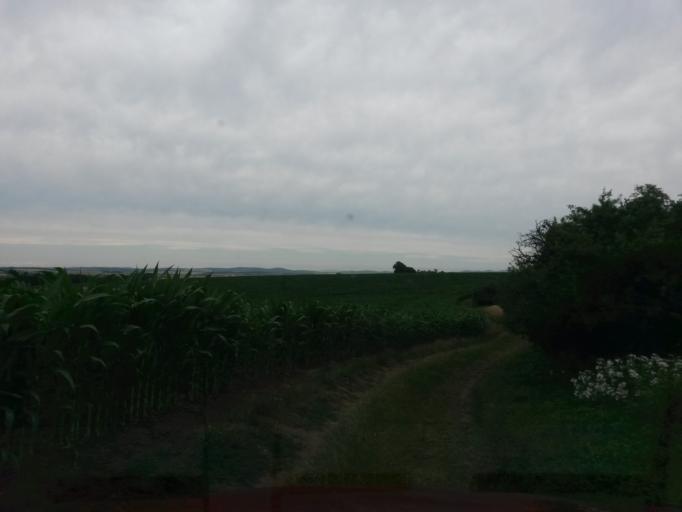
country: SK
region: Nitriansky
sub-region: Okres Nitra
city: Nitra
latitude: 48.3447
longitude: 17.9850
